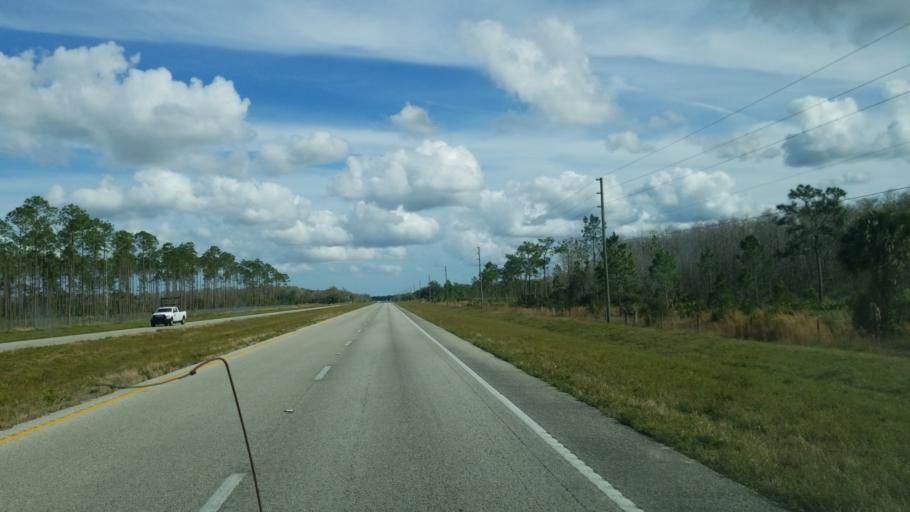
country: US
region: Florida
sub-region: Osceola County
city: Saint Cloud
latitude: 28.1375
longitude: -81.0374
